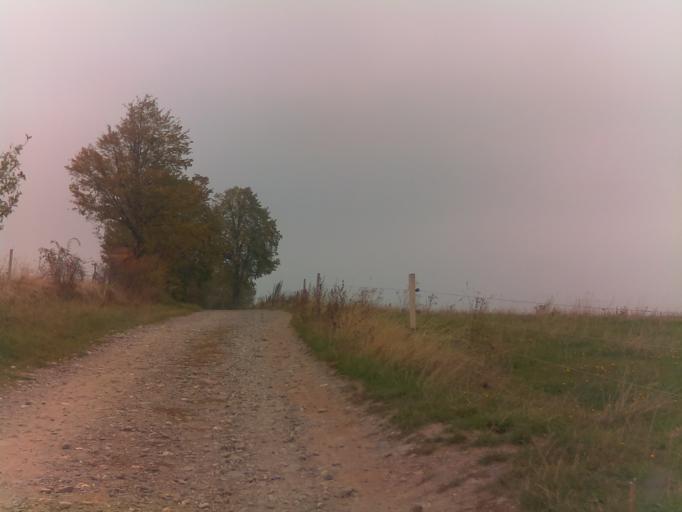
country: DE
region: Thuringia
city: Oberhain
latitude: 50.6375
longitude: 11.1285
